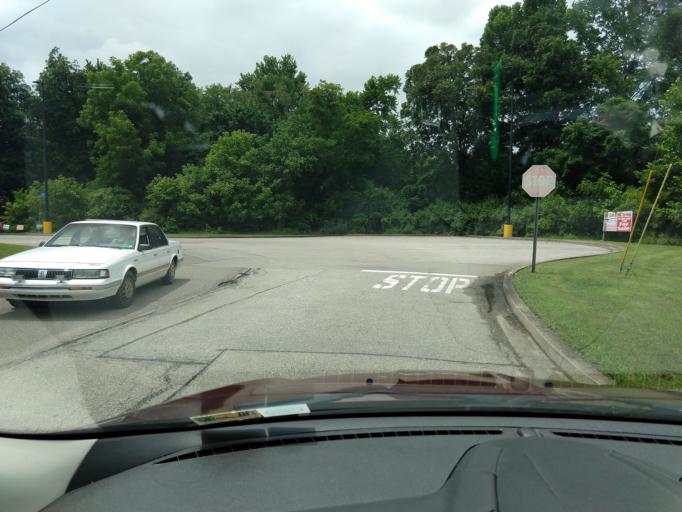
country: US
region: West Virginia
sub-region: Jackson County
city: Ripley
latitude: 38.8305
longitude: -81.7218
